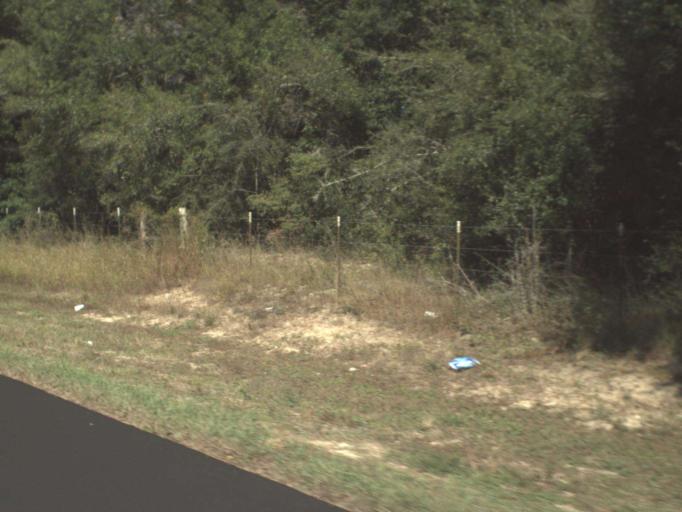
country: US
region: Florida
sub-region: Walton County
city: DeFuniak Springs
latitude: 30.7843
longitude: -86.1742
